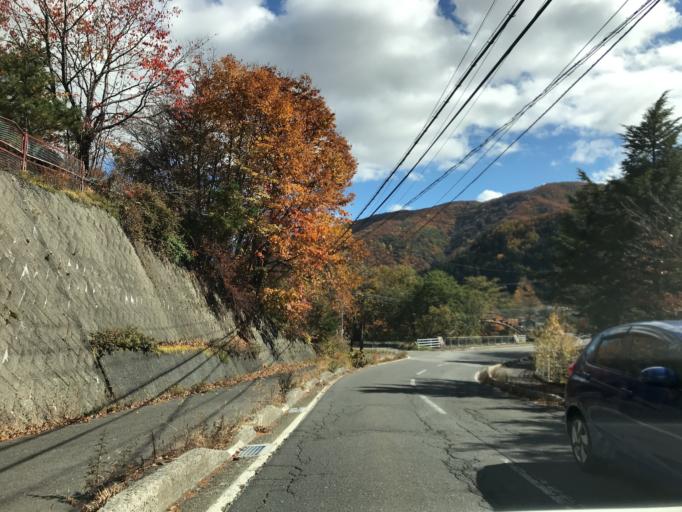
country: JP
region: Nagano
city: Toyoshina
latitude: 36.1251
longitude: 137.6511
